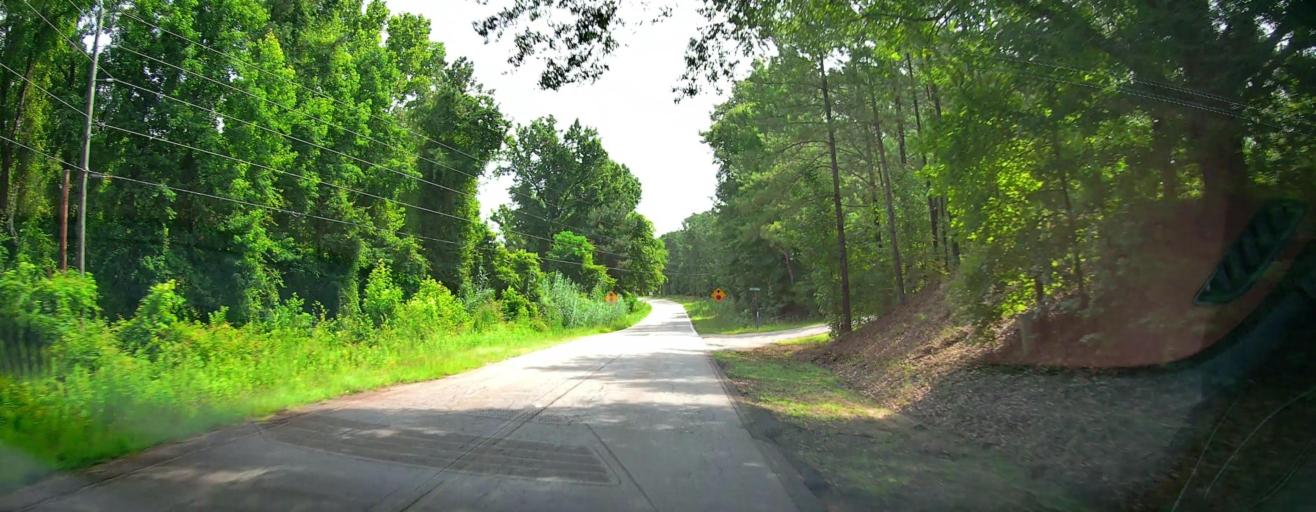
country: US
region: Georgia
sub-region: Peach County
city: Byron
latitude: 32.6051
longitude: -83.7921
